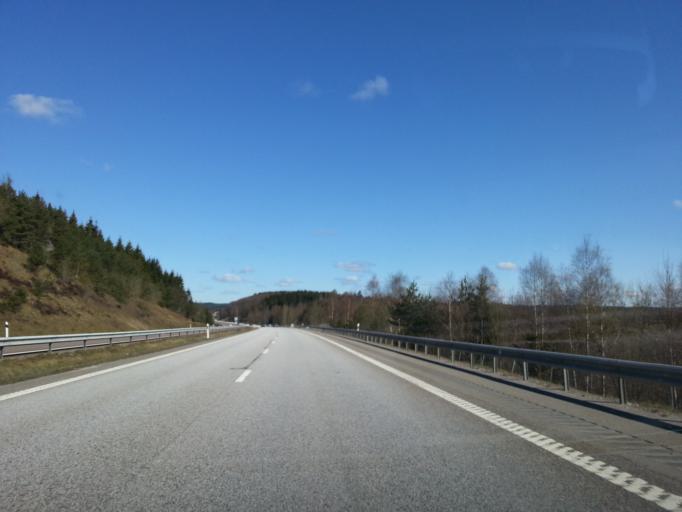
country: SE
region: Vaestra Goetaland
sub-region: Uddevalla Kommun
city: Ljungskile
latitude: 58.1870
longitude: 11.9091
